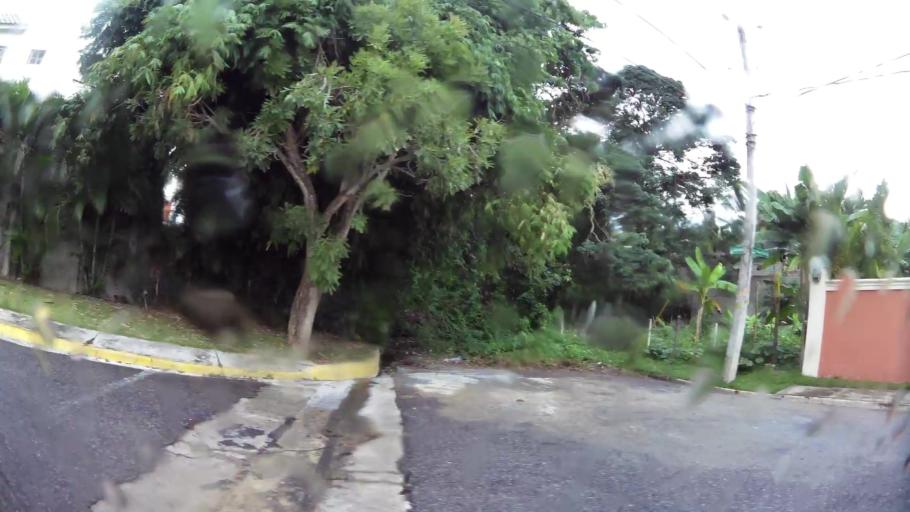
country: DO
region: Nacional
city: La Agustina
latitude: 18.5113
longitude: -69.9383
